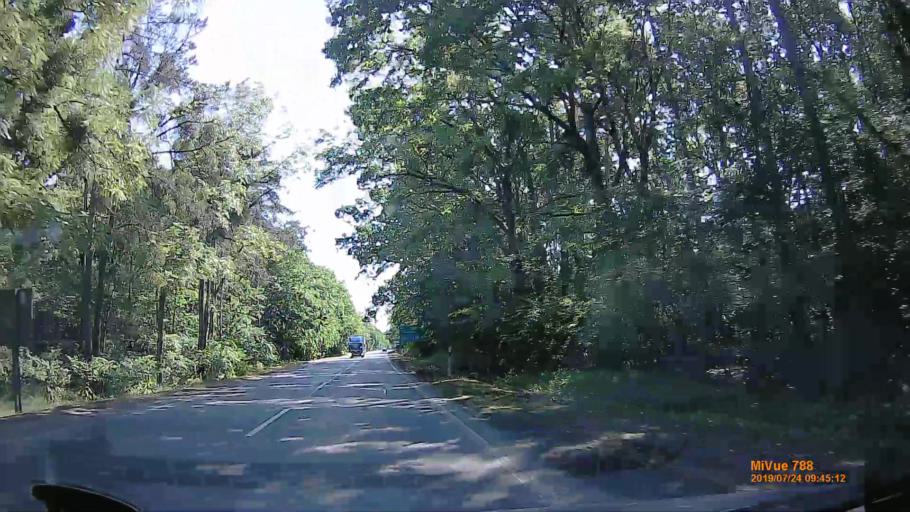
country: HU
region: Szabolcs-Szatmar-Bereg
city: Baktaloranthaza
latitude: 47.9848
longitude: 22.0643
